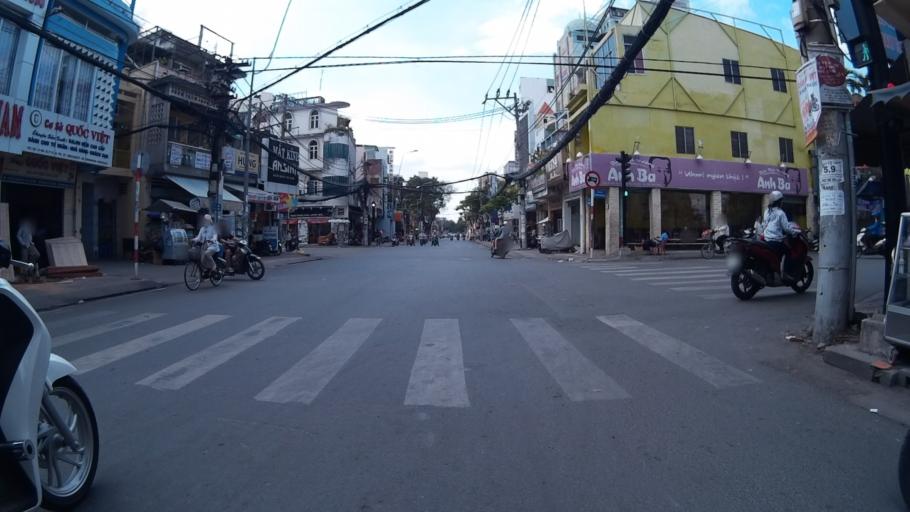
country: VN
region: Ho Chi Minh City
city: Quan Phu Nhuan
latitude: 10.7916
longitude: 106.6718
